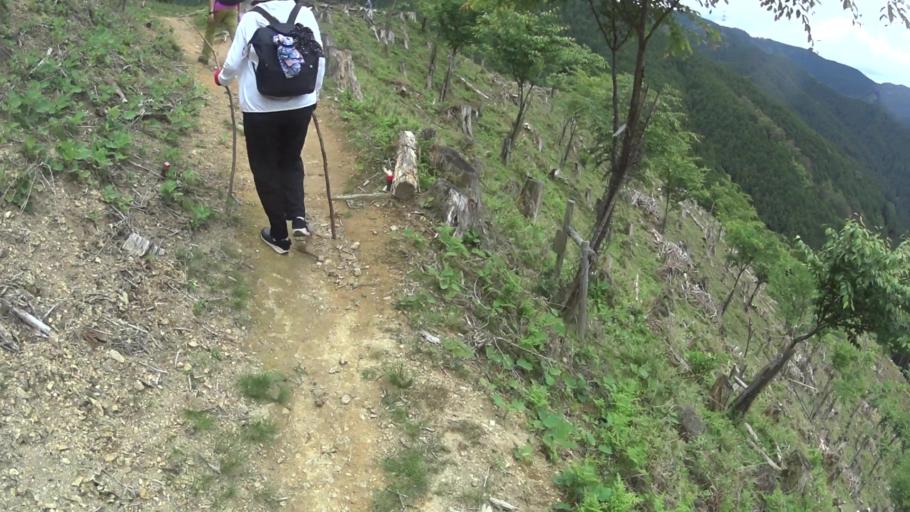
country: JP
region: Nara
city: Yoshino-cho
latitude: 34.3391
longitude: 135.8816
